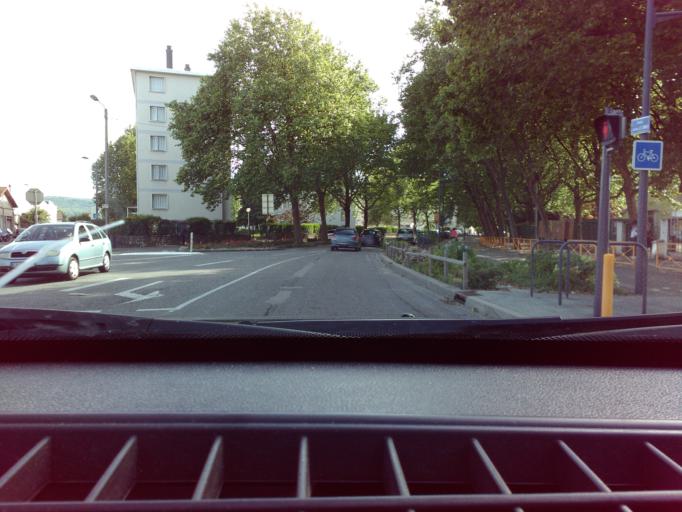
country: FR
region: Rhone-Alpes
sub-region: Departement de l'Isere
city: Saint-Martin-d'Heres
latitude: 45.1683
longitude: 5.7440
